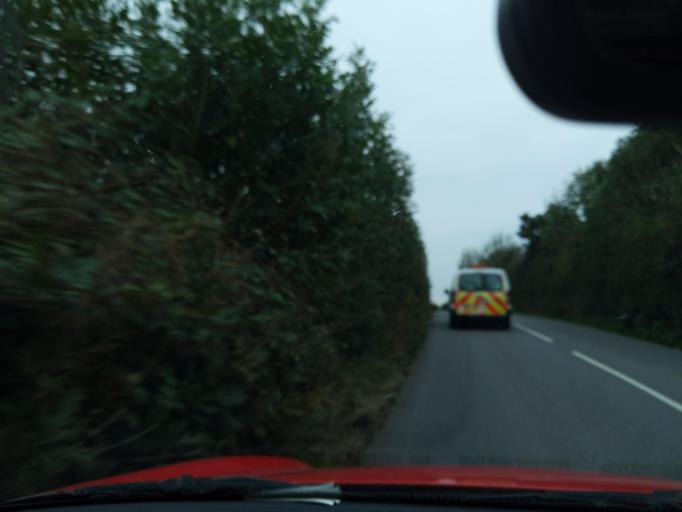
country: GB
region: England
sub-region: Devon
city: Great Torrington
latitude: 50.8644
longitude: -4.0688
